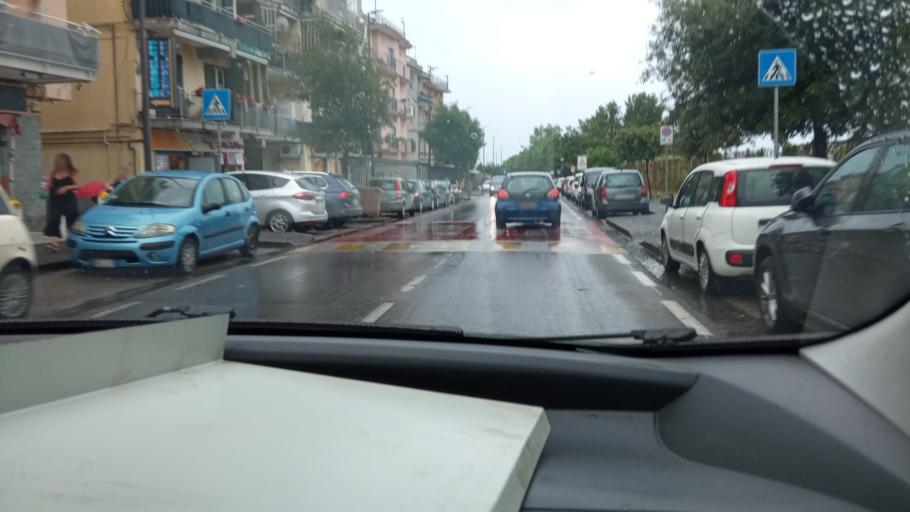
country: IT
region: Campania
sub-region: Provincia di Napoli
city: Pozzuoli
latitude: 40.8363
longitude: 14.1159
